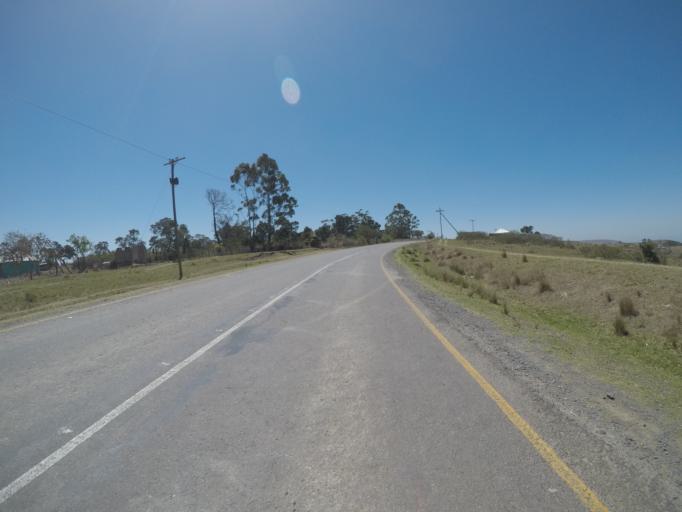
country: ZA
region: Eastern Cape
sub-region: OR Tambo District Municipality
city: Mthatha
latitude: -31.8987
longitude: 28.9363
